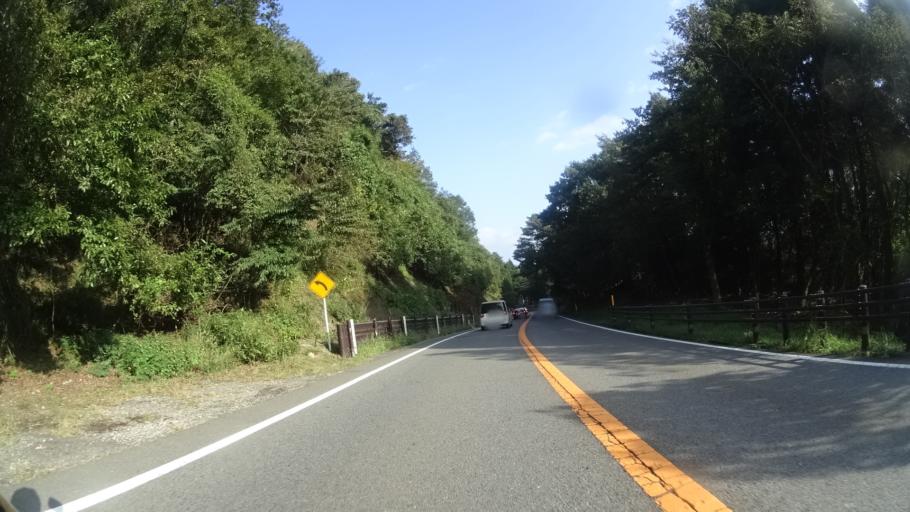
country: JP
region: Oita
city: Tsukawaki
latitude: 33.2532
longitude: 131.3026
